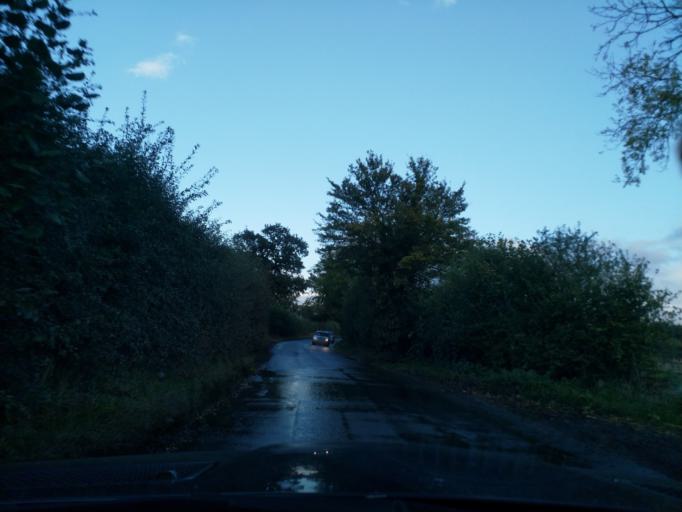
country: GB
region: England
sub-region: Solihull
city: Knowle
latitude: 52.3482
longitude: -1.7154
